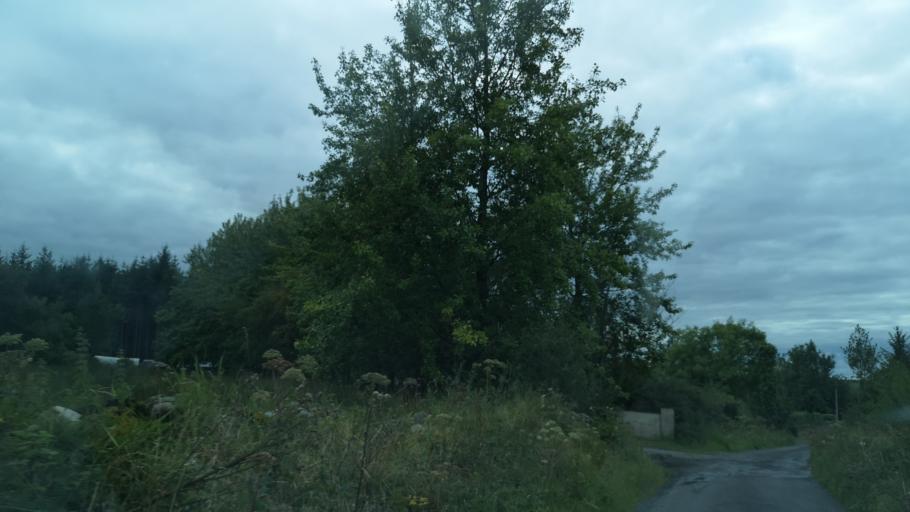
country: IE
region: Connaught
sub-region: County Galway
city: Loughrea
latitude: 53.1385
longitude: -8.5259
